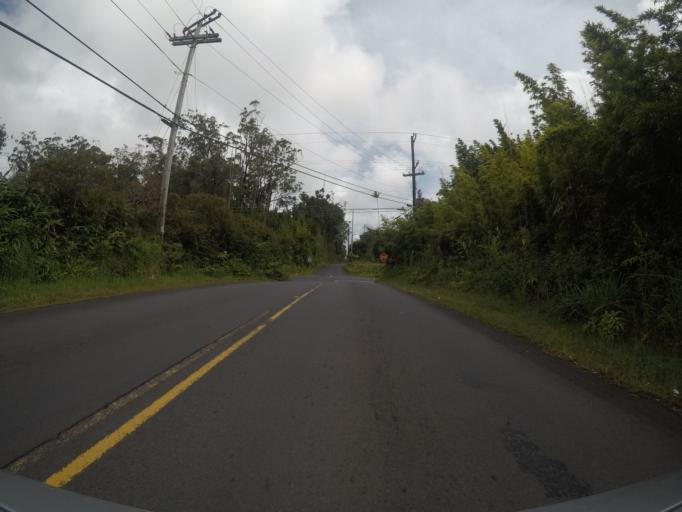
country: US
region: Hawaii
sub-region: Hawaii County
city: Fern Acres
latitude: 19.4861
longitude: -155.1525
